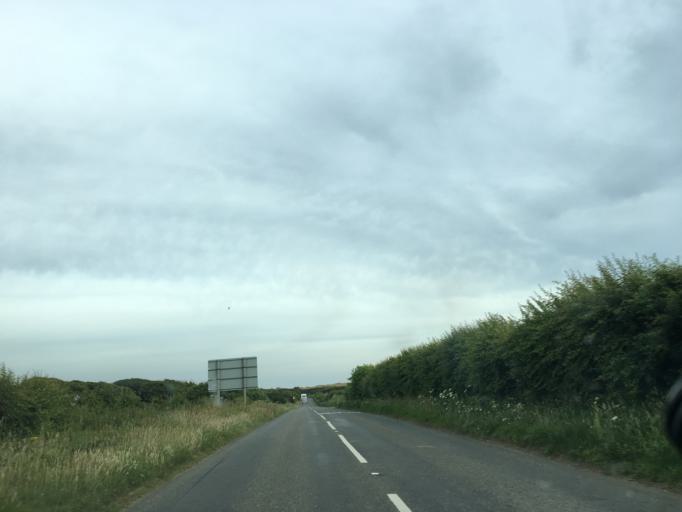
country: GB
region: England
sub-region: Isle of Wight
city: Shalfleet
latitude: 50.6498
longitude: -1.4494
